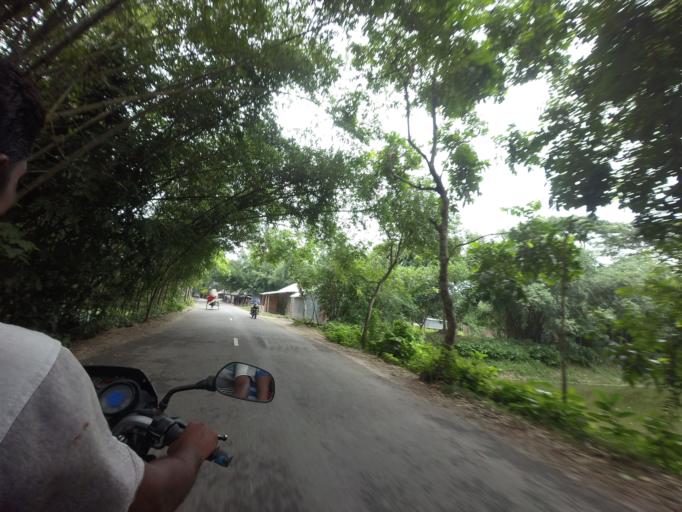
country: BD
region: Khulna
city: Kalia
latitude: 23.1563
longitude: 89.6445
